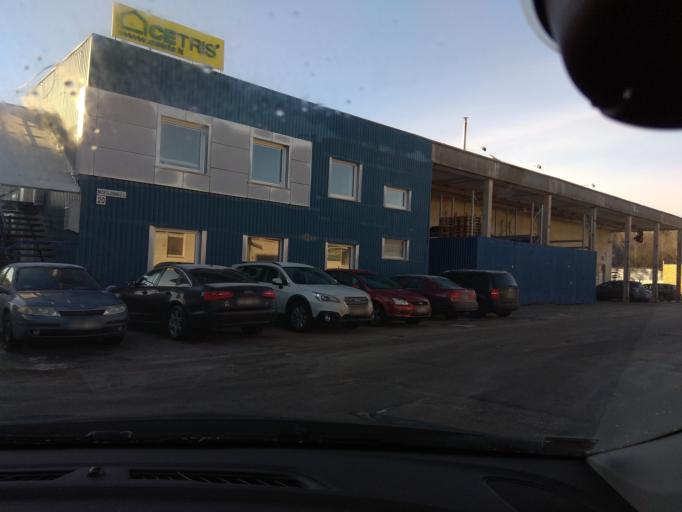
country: LT
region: Vilnius County
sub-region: Vilnius
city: Fabijoniskes
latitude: 54.7530
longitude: 25.2602
